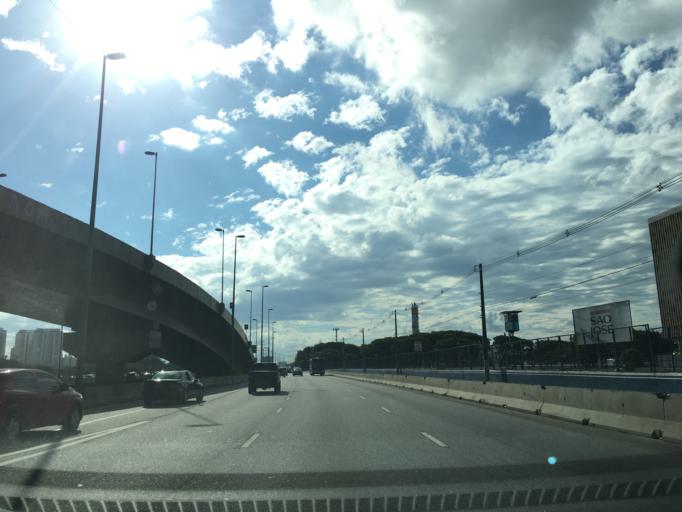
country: BR
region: Sao Paulo
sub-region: Sao Paulo
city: Sao Paulo
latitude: -23.5178
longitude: -46.6382
